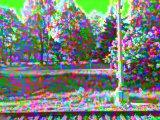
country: SE
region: Soedermanland
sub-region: Flens Kommun
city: Halleforsnas
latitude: 59.1617
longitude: 16.5054
